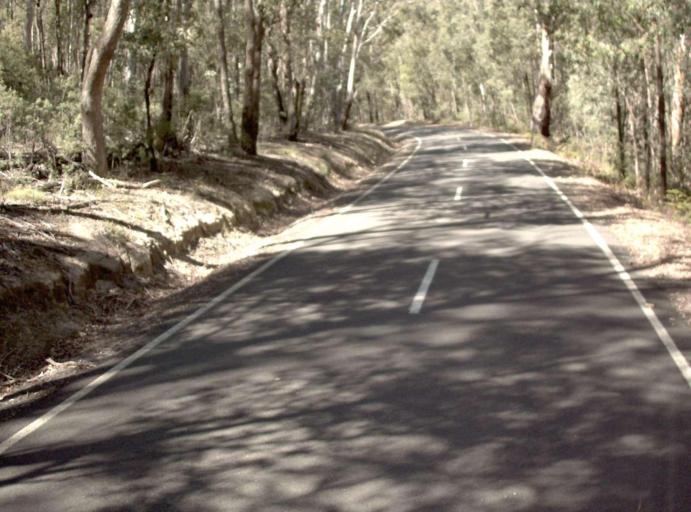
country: AU
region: New South Wales
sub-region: Bombala
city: Bombala
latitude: -37.1219
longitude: 148.7508
